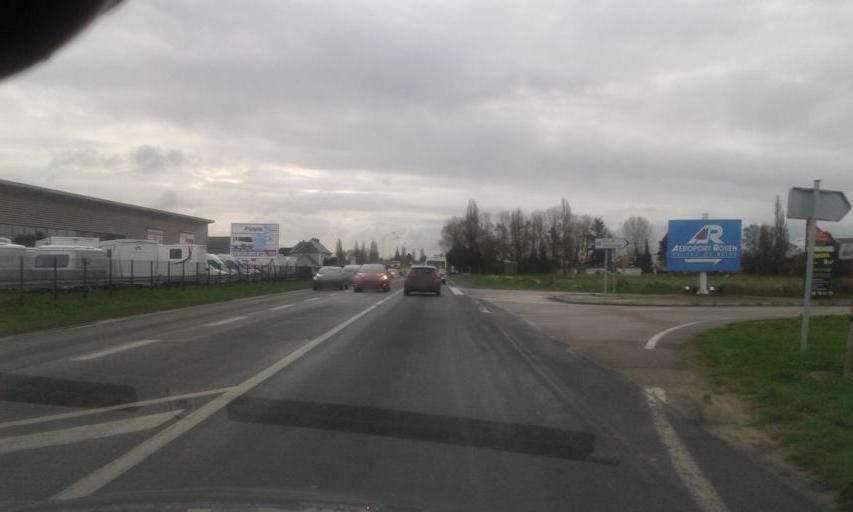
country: FR
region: Haute-Normandie
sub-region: Departement de la Seine-Maritime
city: Boos
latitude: 49.3918
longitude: 1.1936
